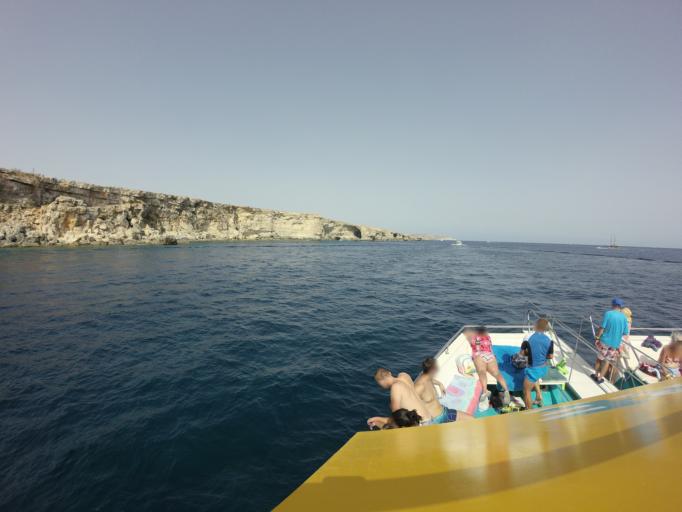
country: MT
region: Il-Mellieha
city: Mellieha
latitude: 35.9908
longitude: 14.3760
